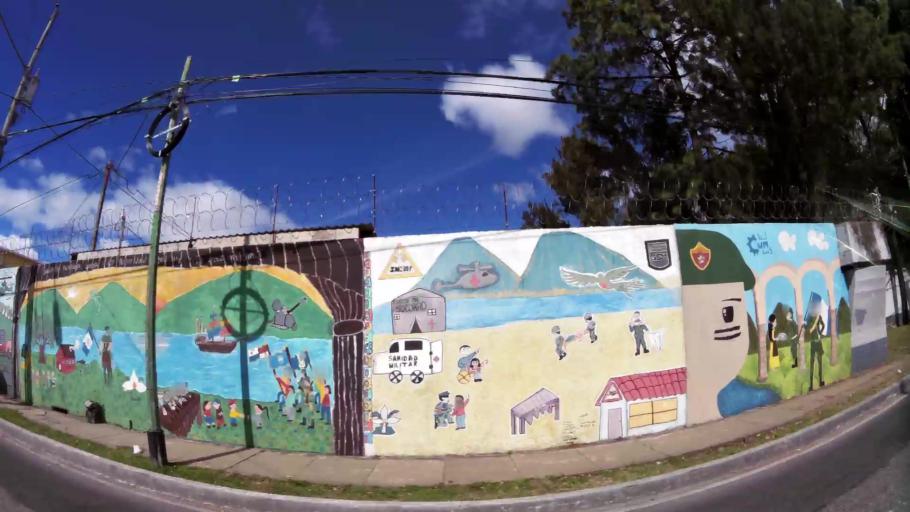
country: GT
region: Guatemala
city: Guatemala City
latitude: 14.6119
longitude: -90.5083
